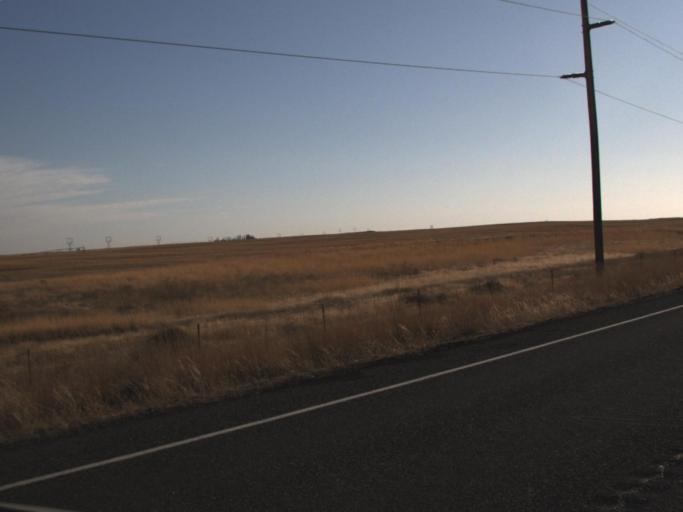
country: US
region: Washington
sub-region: Walla Walla County
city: Burbank
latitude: 46.2812
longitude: -118.7518
